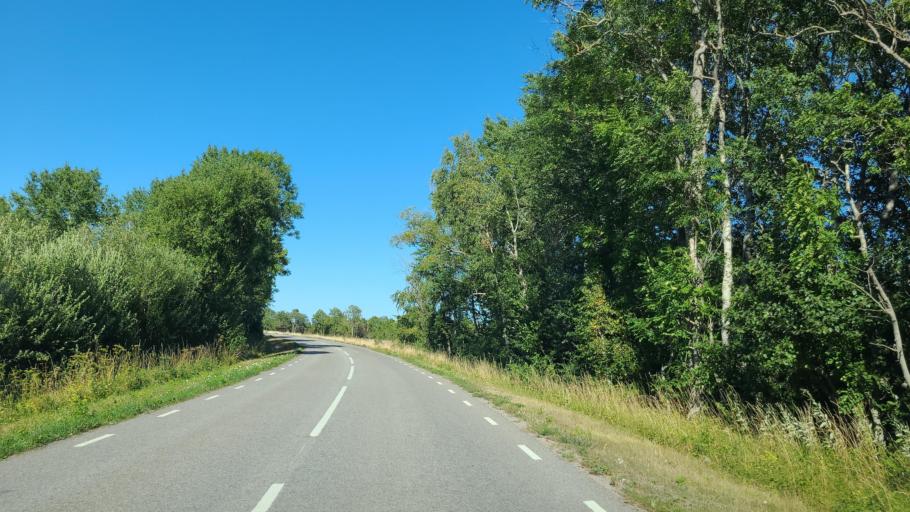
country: SE
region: Kalmar
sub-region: Borgholms Kommun
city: Borgholm
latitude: 56.9760
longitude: 16.8589
